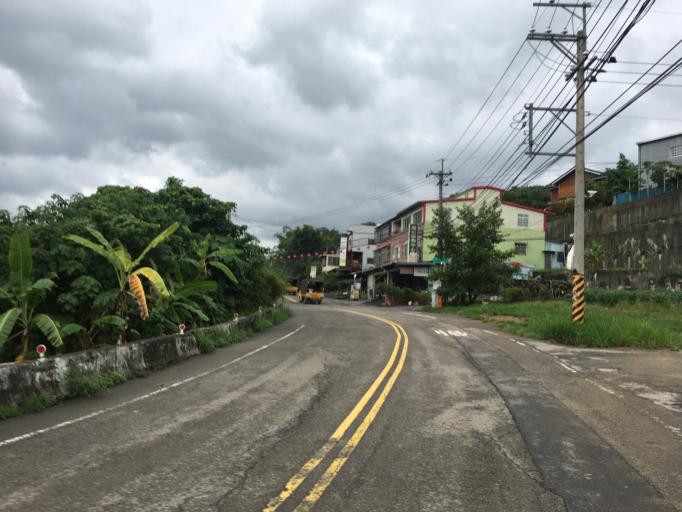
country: TW
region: Taiwan
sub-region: Taichung City
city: Taichung
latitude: 24.0758
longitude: 120.7254
